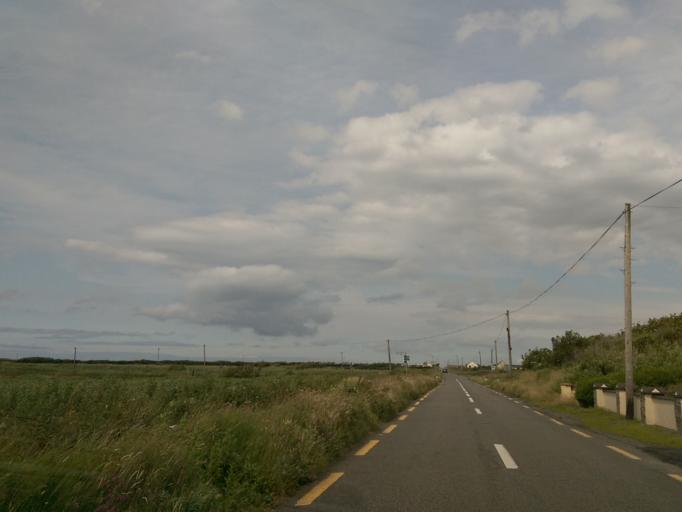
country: IE
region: Munster
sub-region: An Clar
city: Kilrush
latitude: 52.7493
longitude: -9.4788
